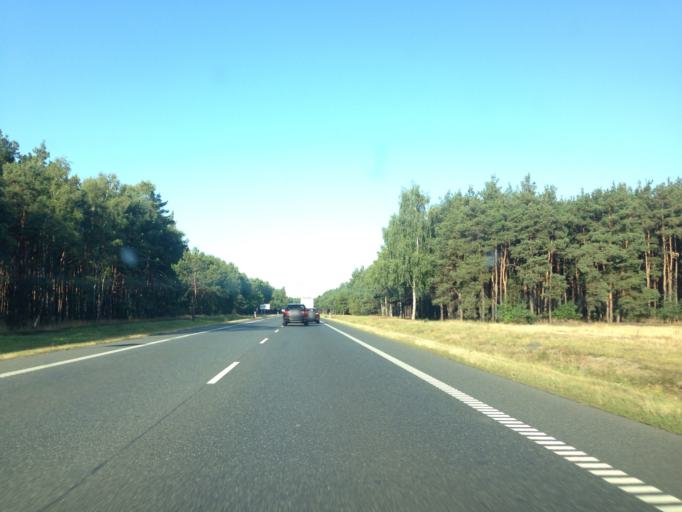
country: PL
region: Kujawsko-Pomorskie
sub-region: Powiat bydgoski
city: Solec Kujawski
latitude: 53.0615
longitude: 18.2009
